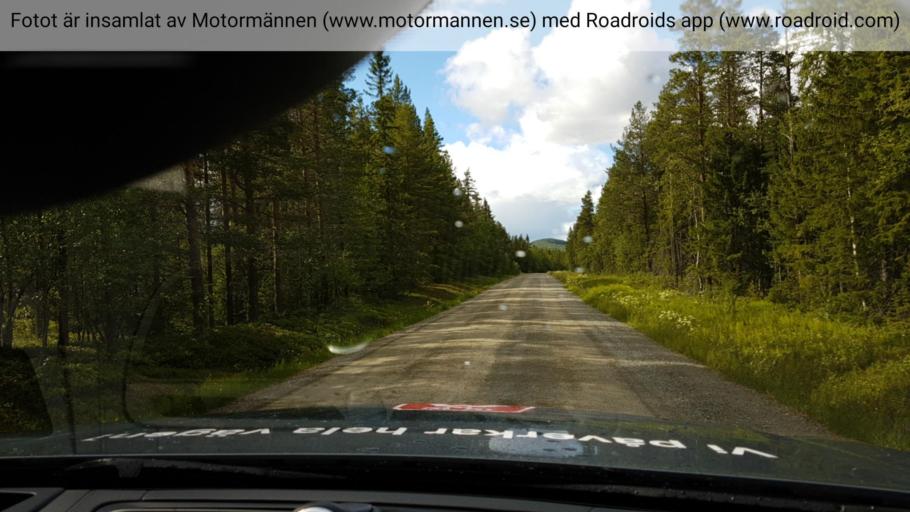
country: SE
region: Jaemtland
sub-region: Bergs Kommun
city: Hoverberg
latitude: 63.0163
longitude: 14.0941
